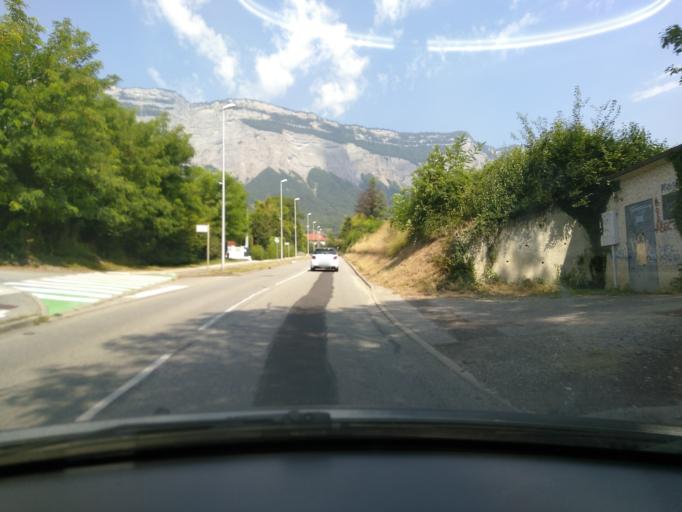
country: FR
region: Rhone-Alpes
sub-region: Departement de l'Isere
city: Montbonnot-Saint-Martin
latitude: 45.2289
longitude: 5.8092
